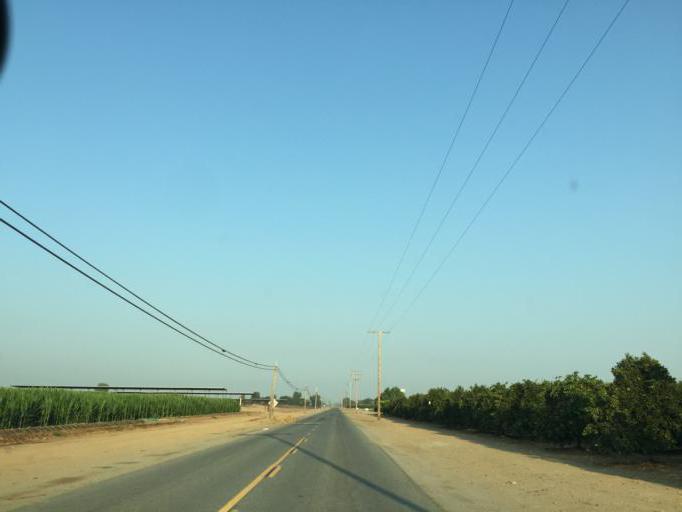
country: US
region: California
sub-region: Tulare County
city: Ivanhoe
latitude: 36.4288
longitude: -119.2967
